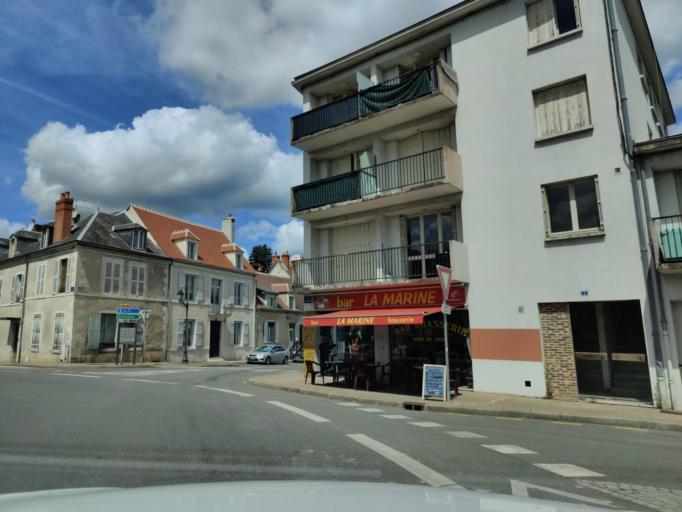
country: FR
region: Centre
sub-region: Departement du Cher
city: Saint-Amand-Montrond
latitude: 46.7185
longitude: 2.5056
